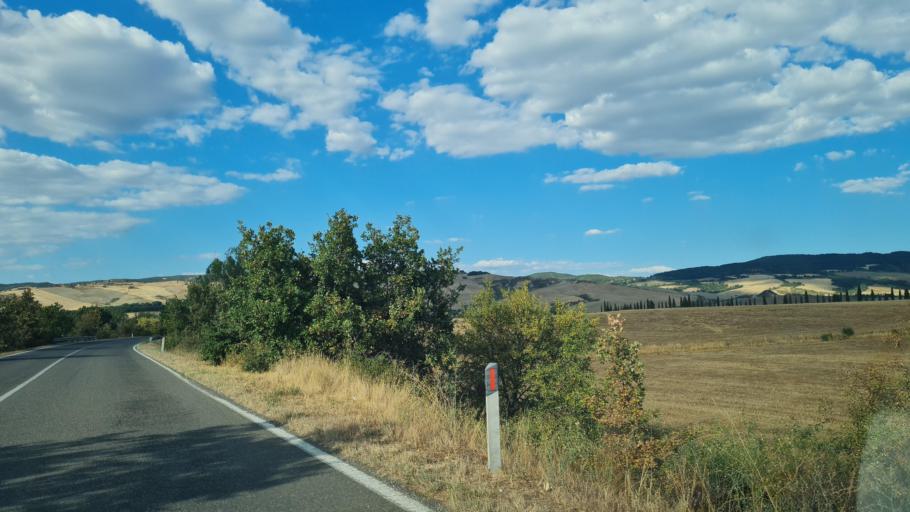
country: IT
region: Tuscany
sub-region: Provincia di Siena
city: Chianciano Terme
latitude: 43.0048
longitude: 11.7302
